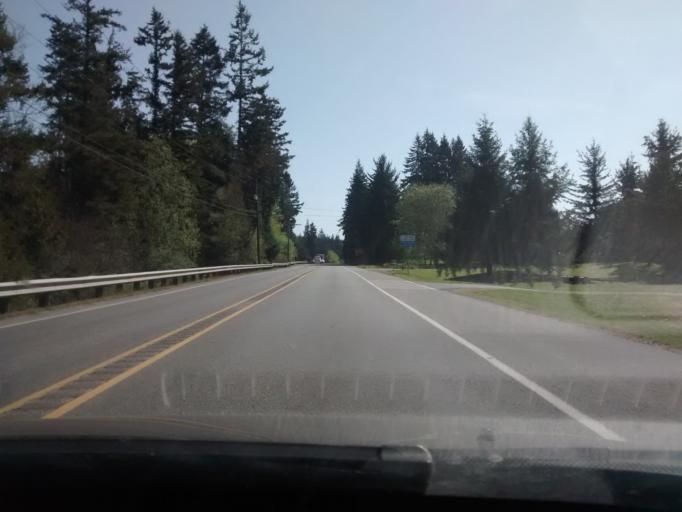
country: US
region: Washington
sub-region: Kitsap County
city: Kingston
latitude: 47.8095
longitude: -122.5280
